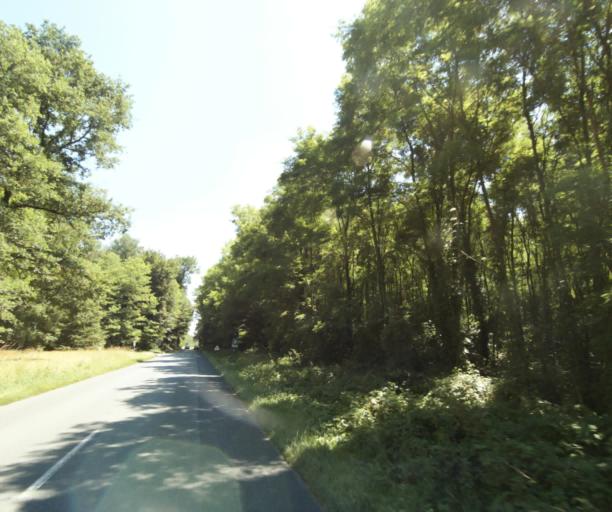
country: FR
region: Ile-de-France
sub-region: Departement de Seine-et-Marne
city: Noisy-sur-Ecole
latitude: 48.3723
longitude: 2.5077
